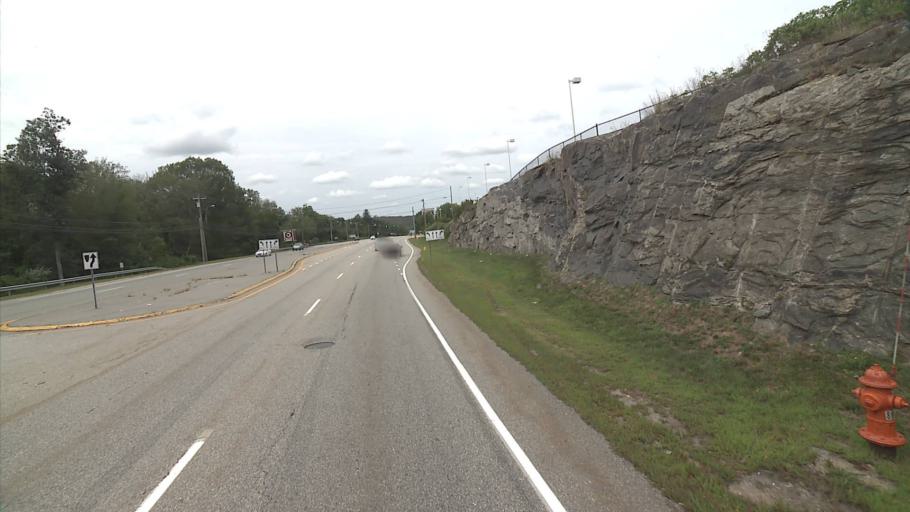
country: US
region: Connecticut
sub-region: New London County
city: Central Waterford
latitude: 41.3780
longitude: -72.1475
